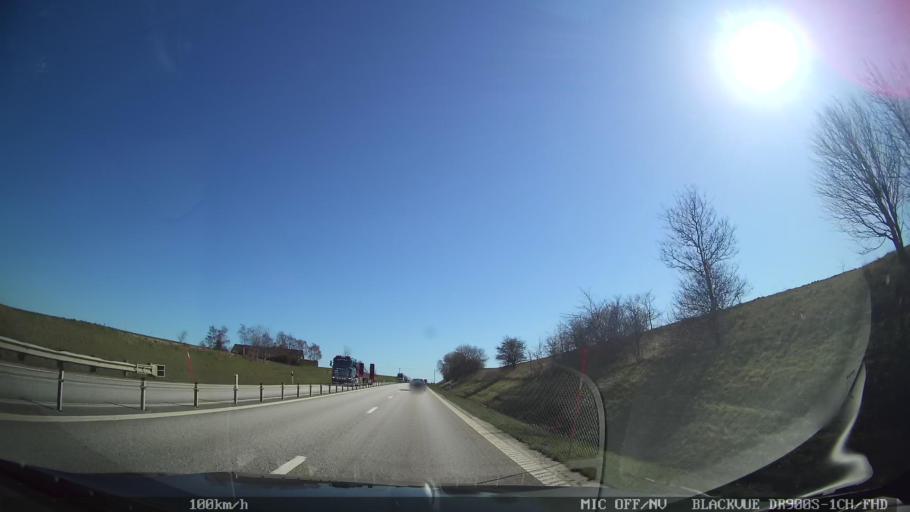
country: SE
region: Skane
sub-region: Skurups Kommun
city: Rydsgard
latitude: 55.4823
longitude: 13.6012
